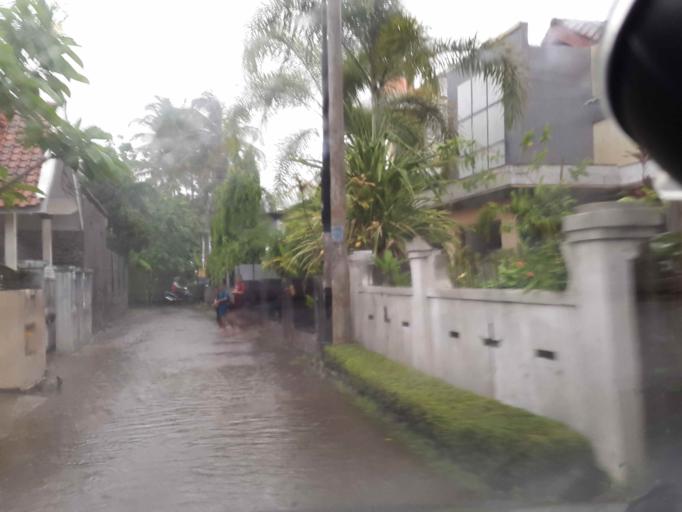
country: ID
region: Central Java
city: Kutoarjo
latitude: -7.7164
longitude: 110.0017
